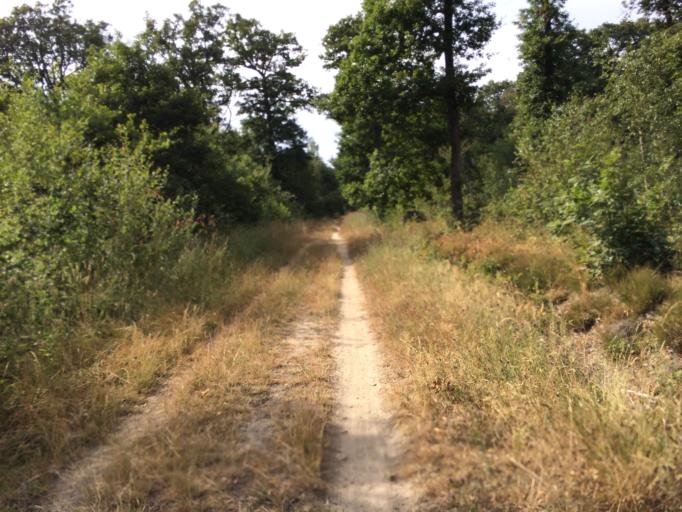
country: FR
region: Ile-de-France
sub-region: Departement de l'Essonne
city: Epinay-sous-Senart
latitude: 48.6768
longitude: 2.5149
